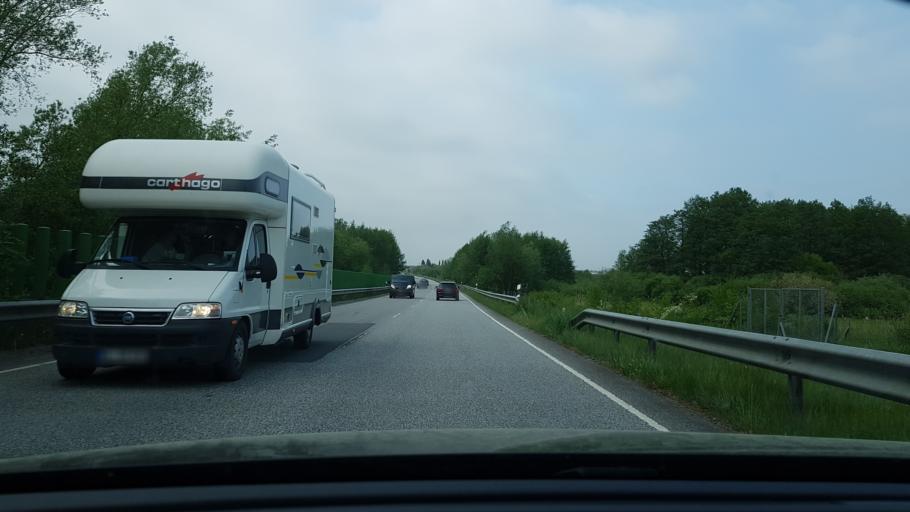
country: DE
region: Schleswig-Holstein
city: Luebeck
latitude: 53.8216
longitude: 10.6925
